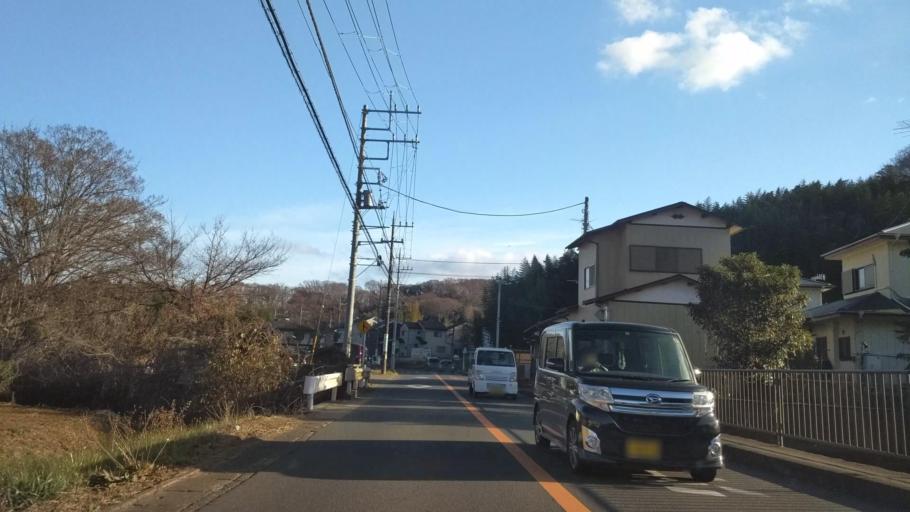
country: JP
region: Kanagawa
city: Oiso
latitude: 35.3450
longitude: 139.2810
